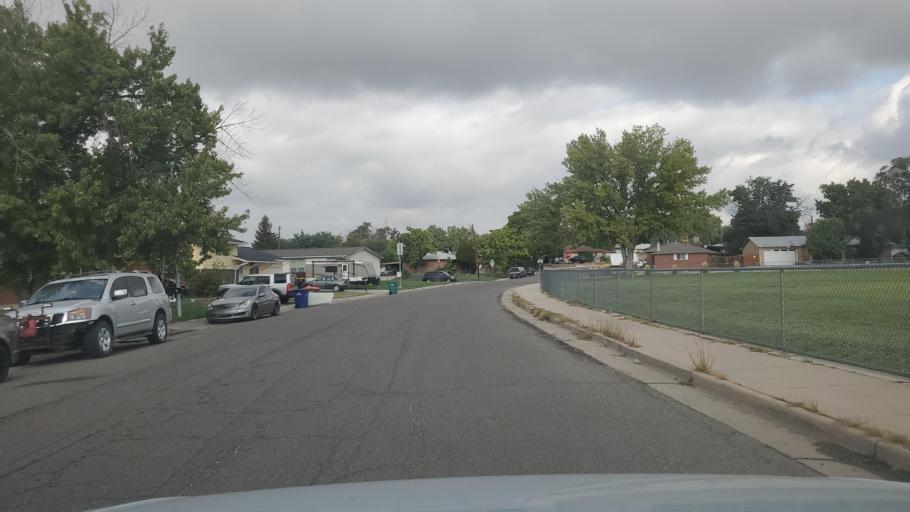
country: US
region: Colorado
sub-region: Adams County
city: Welby
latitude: 39.8470
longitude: -104.9703
